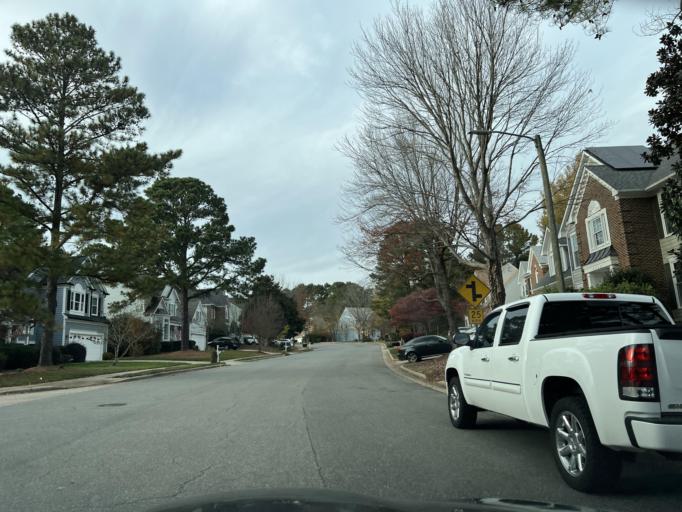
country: US
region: North Carolina
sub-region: Wake County
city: Wake Forest
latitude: 35.8935
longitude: -78.5947
